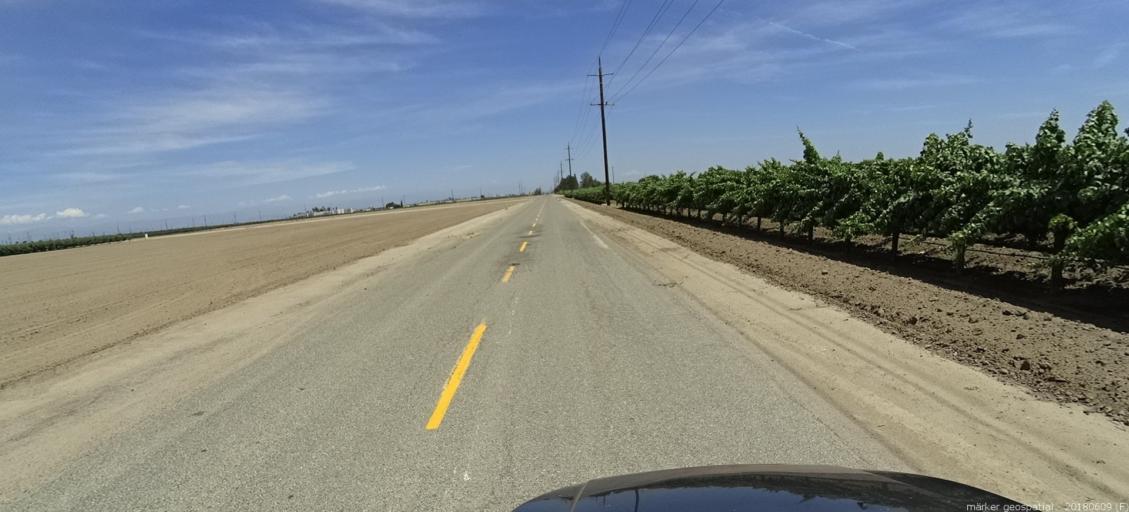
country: US
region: California
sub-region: Madera County
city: Parkwood
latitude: 36.9166
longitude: -120.0636
